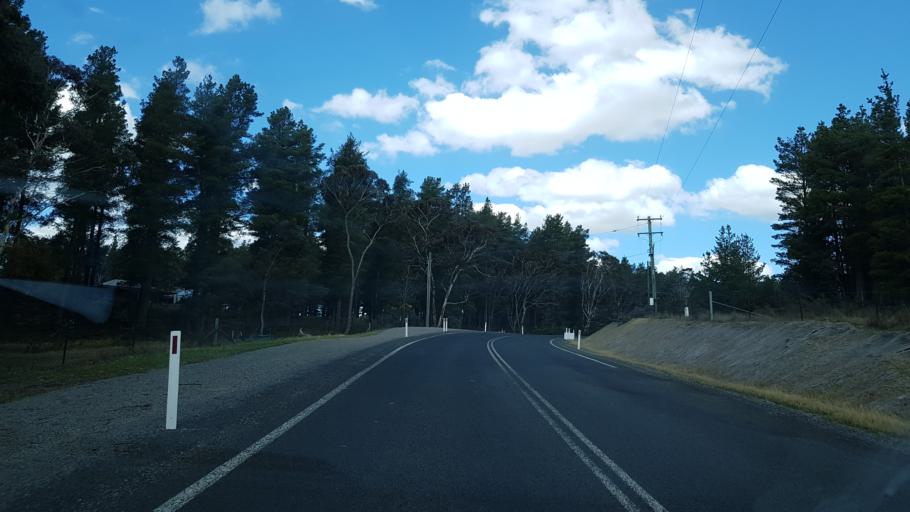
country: AU
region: New South Wales
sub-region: Queanbeyan
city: Queanbeyan
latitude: -35.3898
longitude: 149.2938
